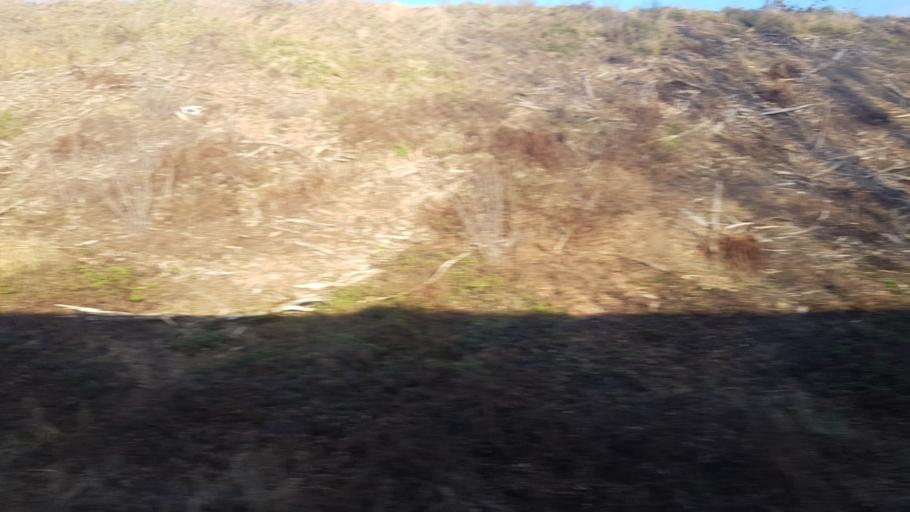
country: FR
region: Lorraine
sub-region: Departement des Vosges
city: Urimenil
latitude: 48.0917
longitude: 6.4355
